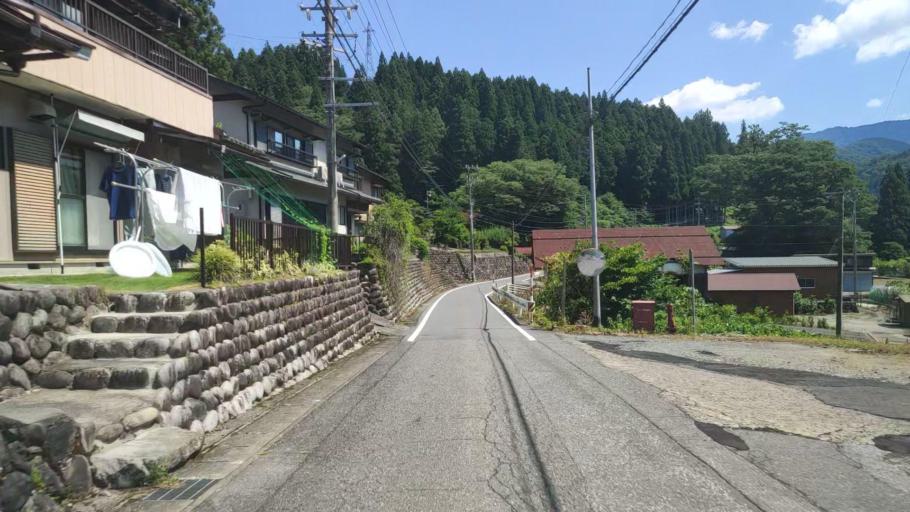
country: JP
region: Gifu
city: Godo
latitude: 35.6701
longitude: 136.5775
